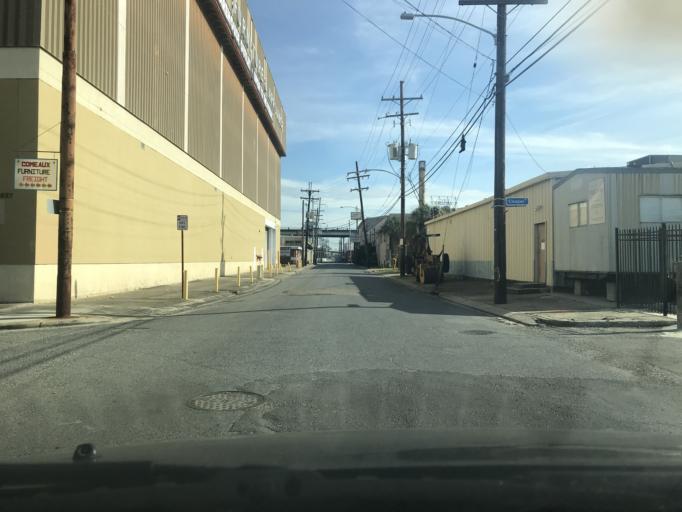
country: US
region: Louisiana
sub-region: Orleans Parish
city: New Orleans
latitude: 29.9568
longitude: -90.0972
